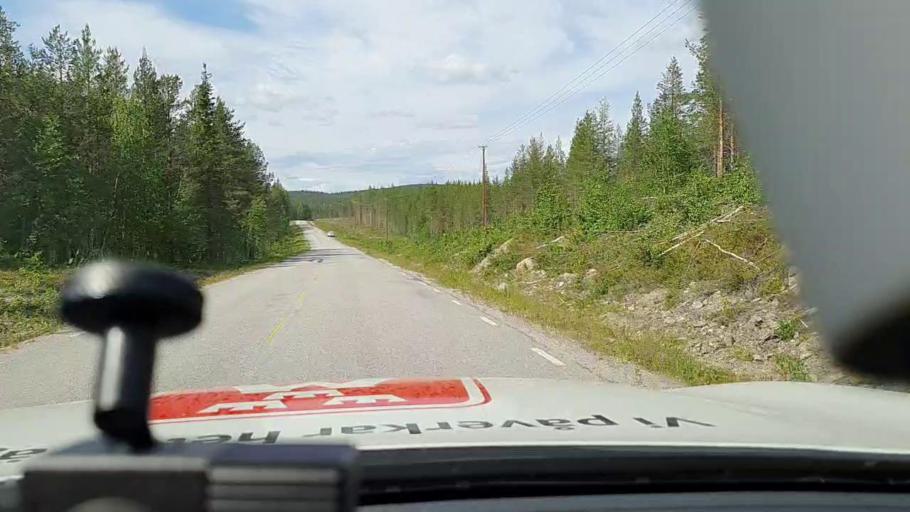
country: SE
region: Norrbotten
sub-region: Jokkmokks Kommun
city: Jokkmokk
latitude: 66.6238
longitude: 19.6700
